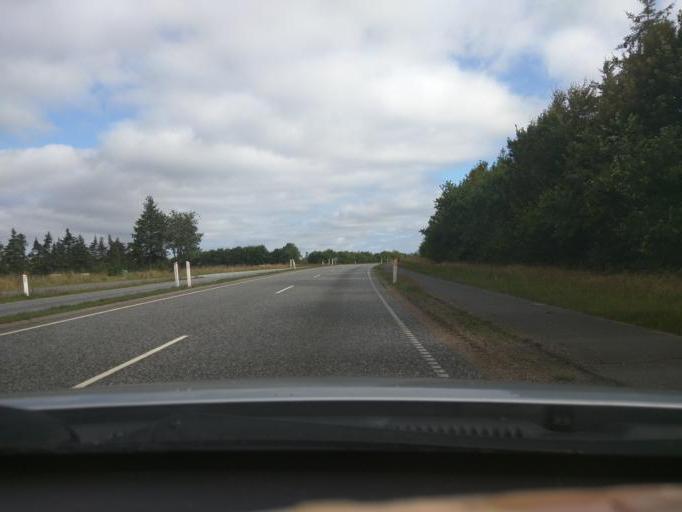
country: DK
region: Central Jutland
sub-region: Viborg Kommune
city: Viborg
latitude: 56.4070
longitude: 9.3716
